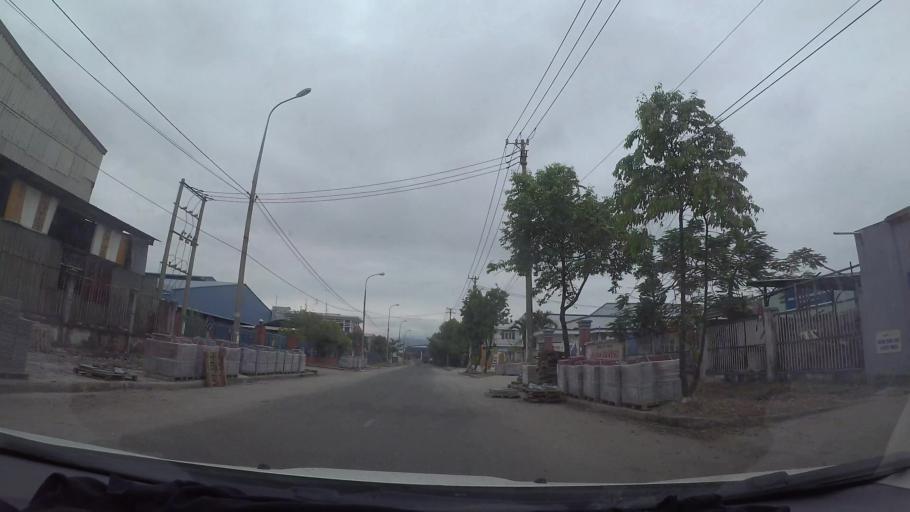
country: VN
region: Da Nang
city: Lien Chieu
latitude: 16.0858
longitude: 108.1383
